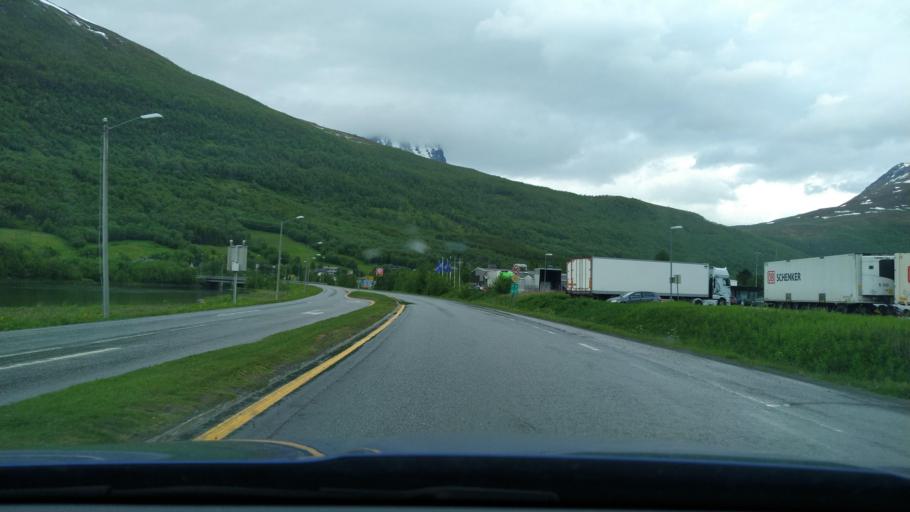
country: NO
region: Troms
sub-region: Balsfjord
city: Storsteinnes
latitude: 69.2153
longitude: 19.5518
